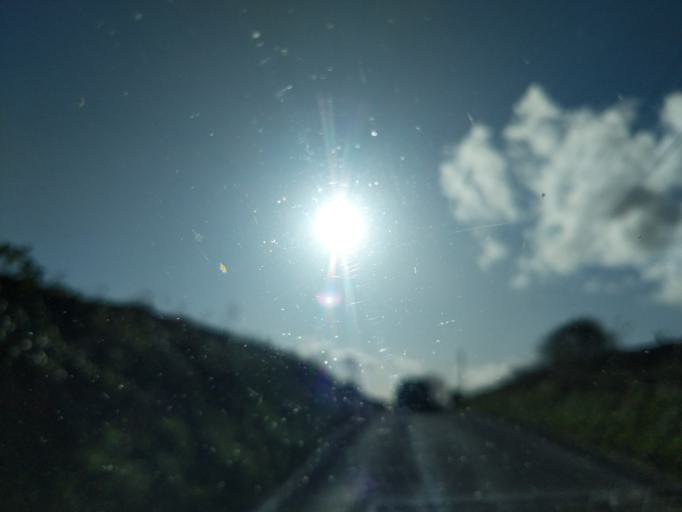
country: GB
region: Scotland
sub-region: Dumfries and Galloway
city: Dalbeattie
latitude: 54.9914
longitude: -3.8409
